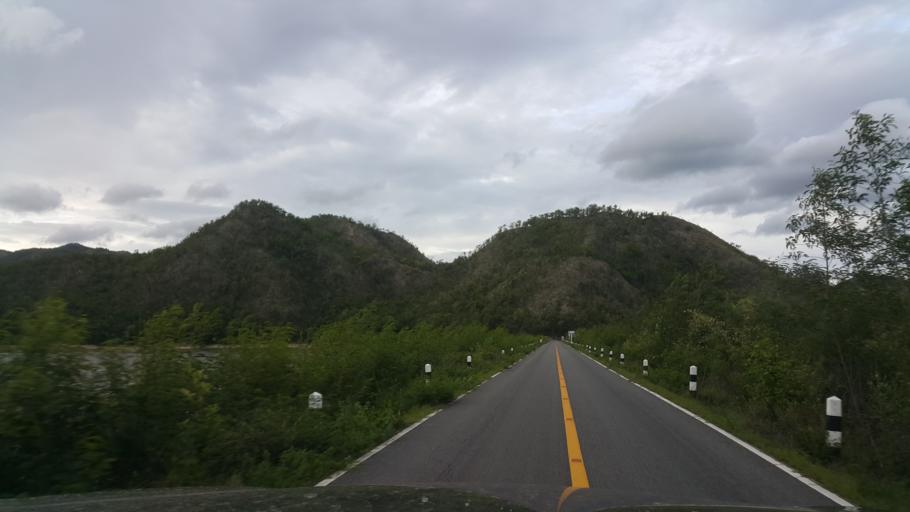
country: TH
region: Sukhothai
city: Thung Saliam
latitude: 17.1773
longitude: 99.4815
